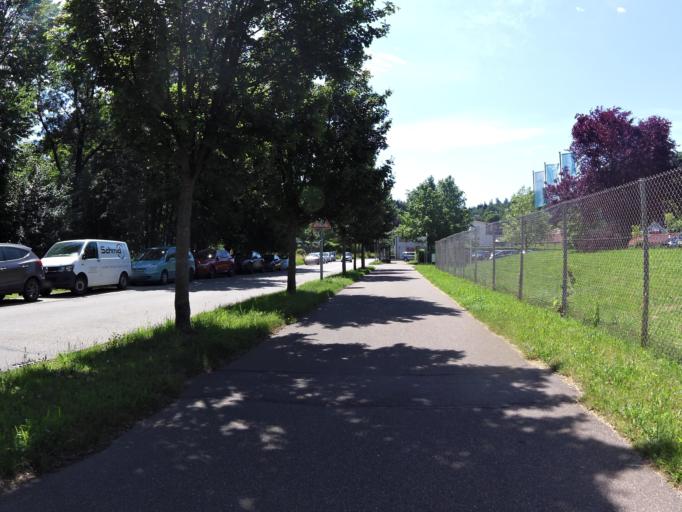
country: DE
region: Baden-Wuerttemberg
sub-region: Freiburg Region
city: Hohberg
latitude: 48.3400
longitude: 7.8922
